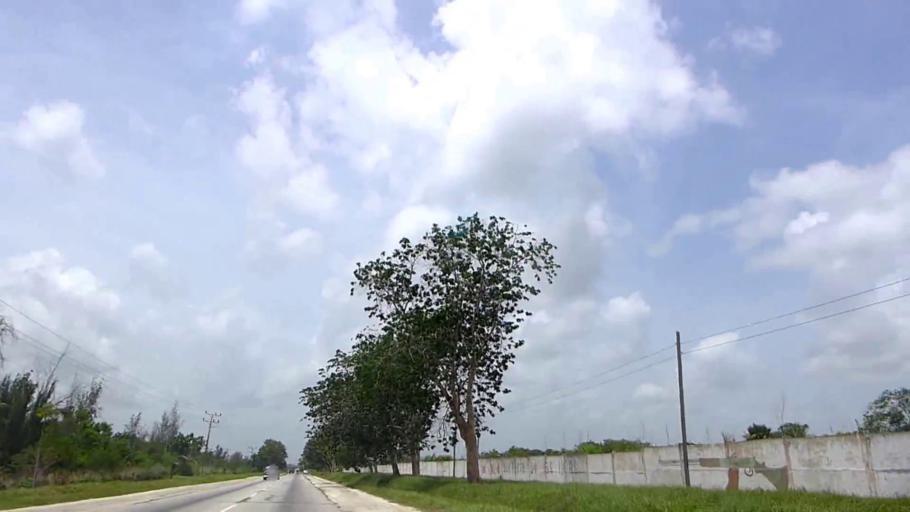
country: CU
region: Holguin
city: Cacocum
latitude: 20.7933
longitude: -76.2993
